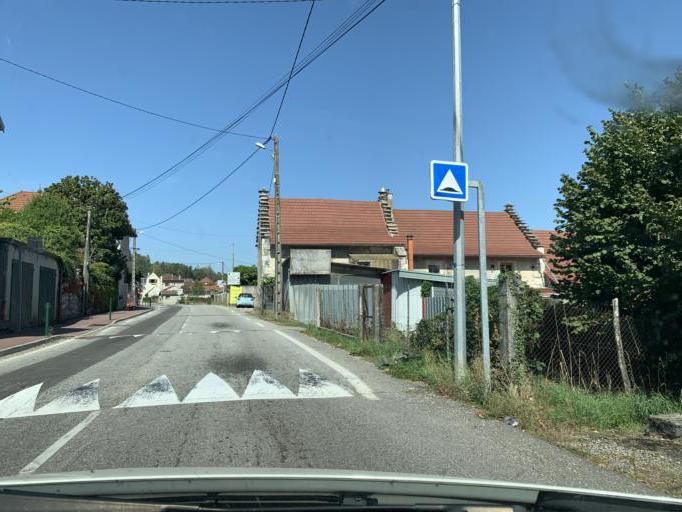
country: FR
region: Rhone-Alpes
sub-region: Departement de la Savoie
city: Yenne
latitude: 45.6752
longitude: 5.6782
